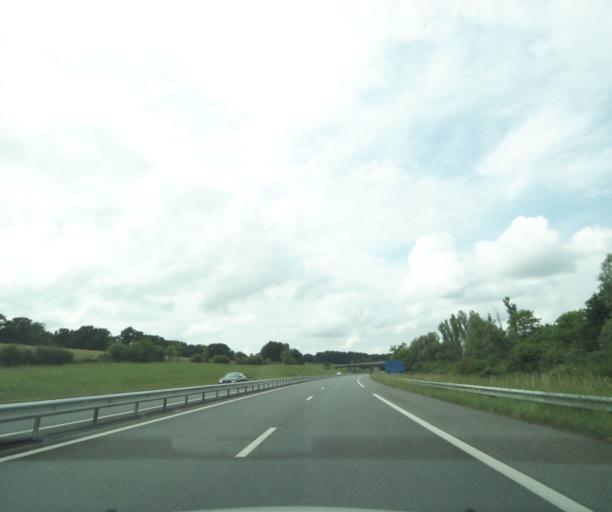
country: FR
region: Centre
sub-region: Departement du Cher
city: Orval
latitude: 46.7286
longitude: 2.4313
